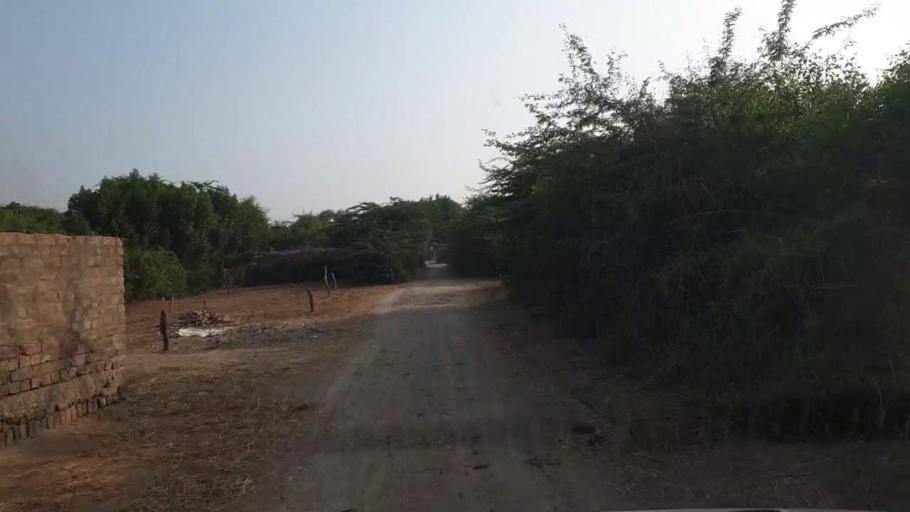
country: PK
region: Sindh
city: Rajo Khanani
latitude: 25.0328
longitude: 68.7772
